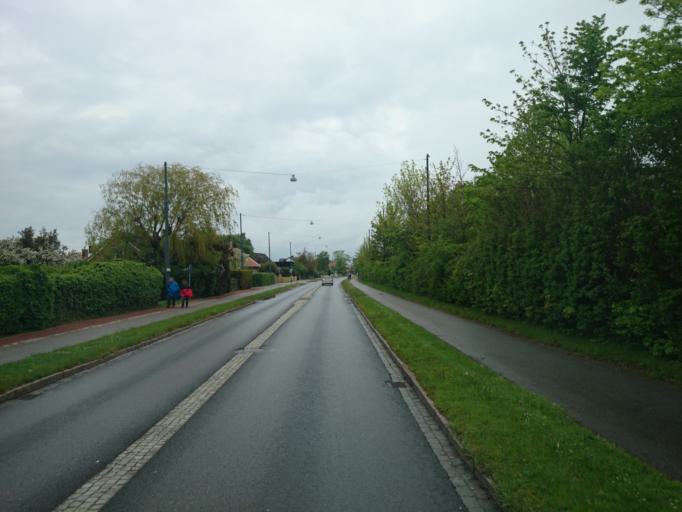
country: SE
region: Skane
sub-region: Malmo
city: Bunkeflostrand
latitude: 55.5725
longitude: 12.9234
